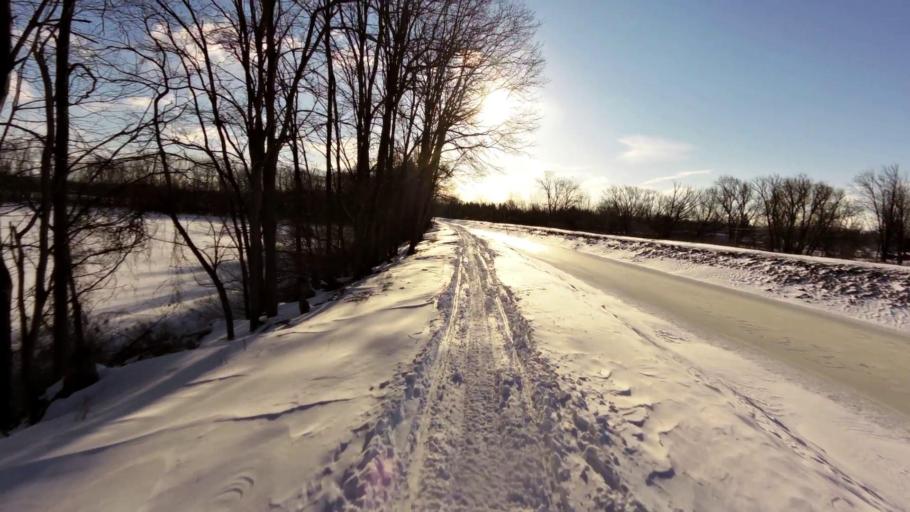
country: US
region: New York
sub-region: Orleans County
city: Albion
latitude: 43.2479
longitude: -78.2098
